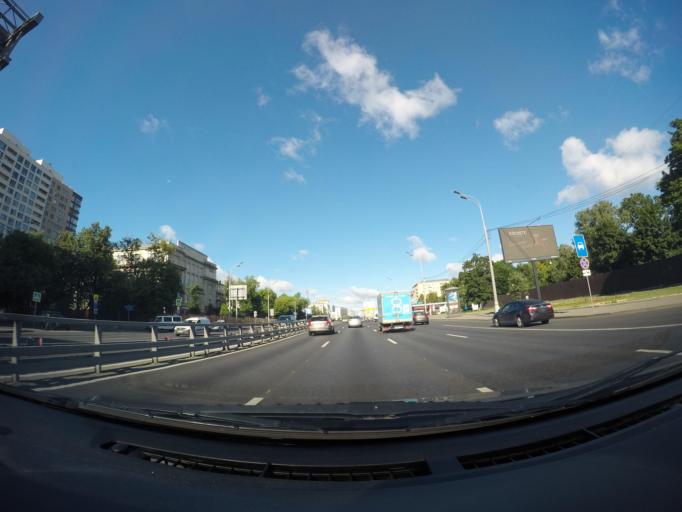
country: RU
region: Moscow
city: Mar'ina Roshcha
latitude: 55.7926
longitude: 37.5997
